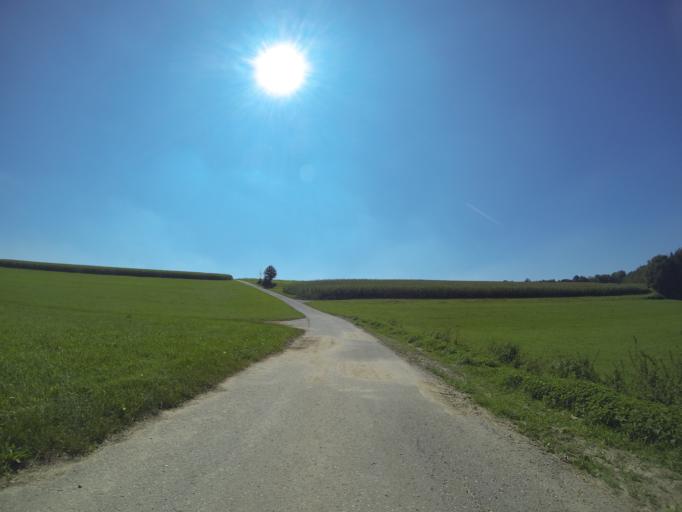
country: DE
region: Baden-Wuerttemberg
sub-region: Tuebingen Region
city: Achstetten
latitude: 48.2541
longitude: 9.9192
